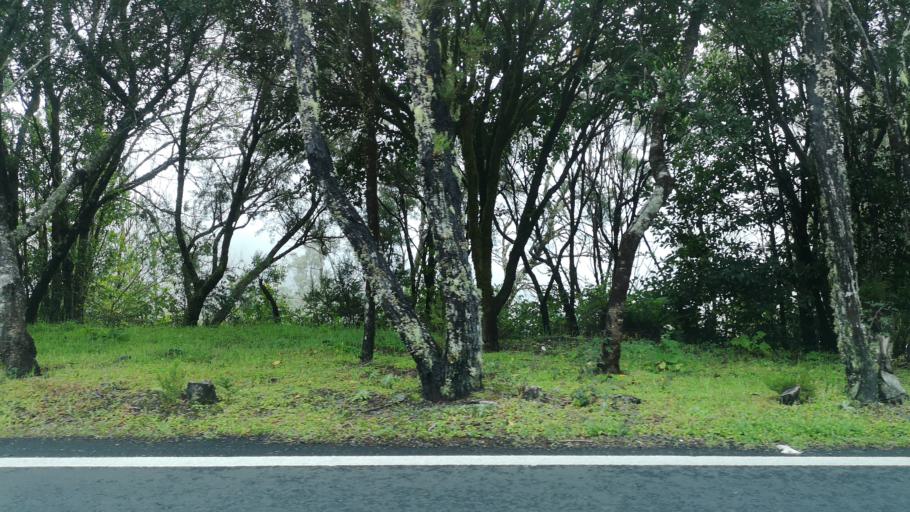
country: ES
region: Canary Islands
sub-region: Provincia de Santa Cruz de Tenerife
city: Vallehermosa
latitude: 28.1287
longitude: -17.2686
